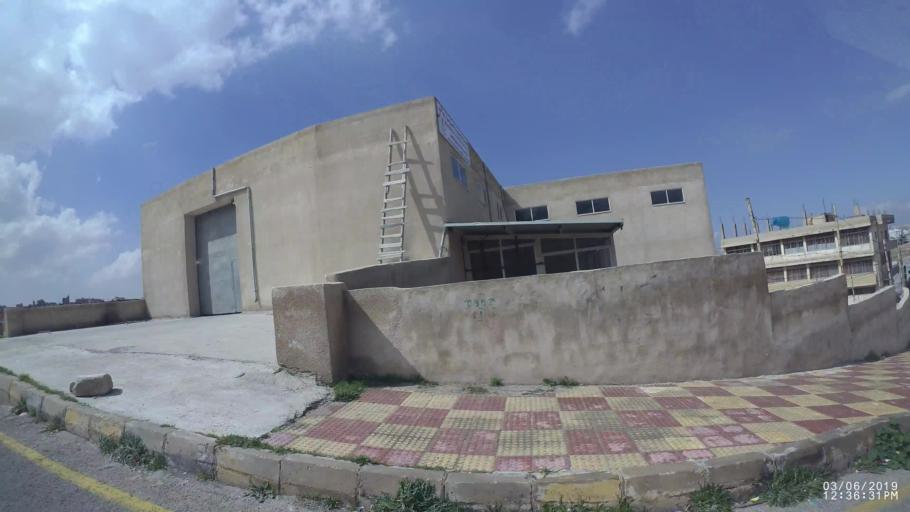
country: JO
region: Zarqa
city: Russeifa
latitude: 31.9913
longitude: 35.9957
